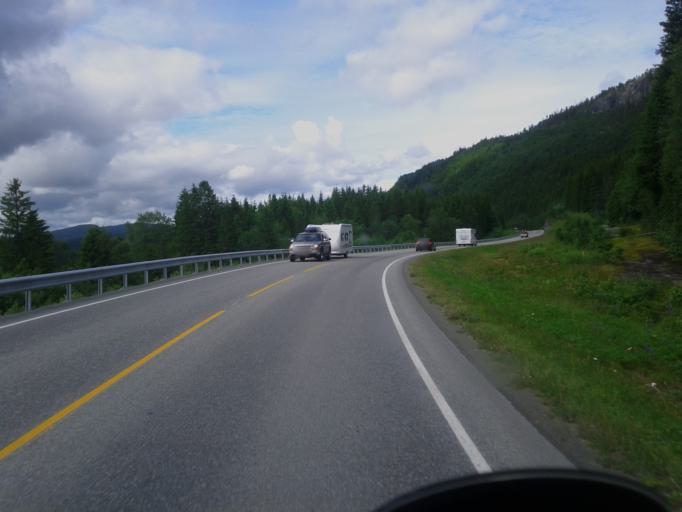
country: NO
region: Nord-Trondelag
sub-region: Grong
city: Grong
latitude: 64.5358
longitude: 12.4400
